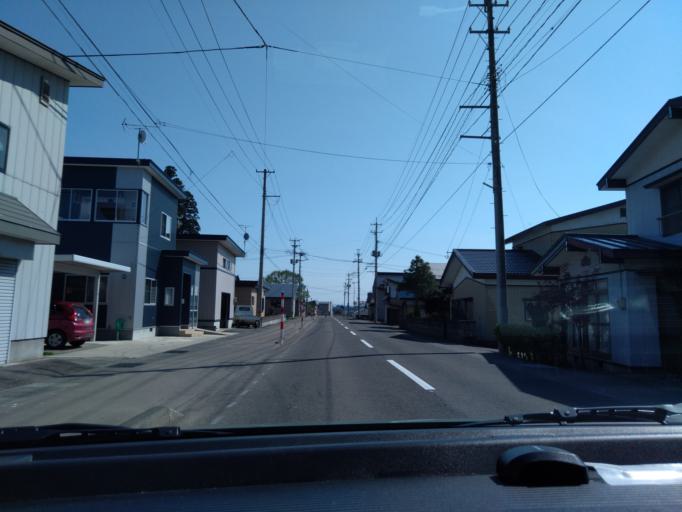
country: JP
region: Akita
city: Omagari
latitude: 39.4552
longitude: 140.5779
